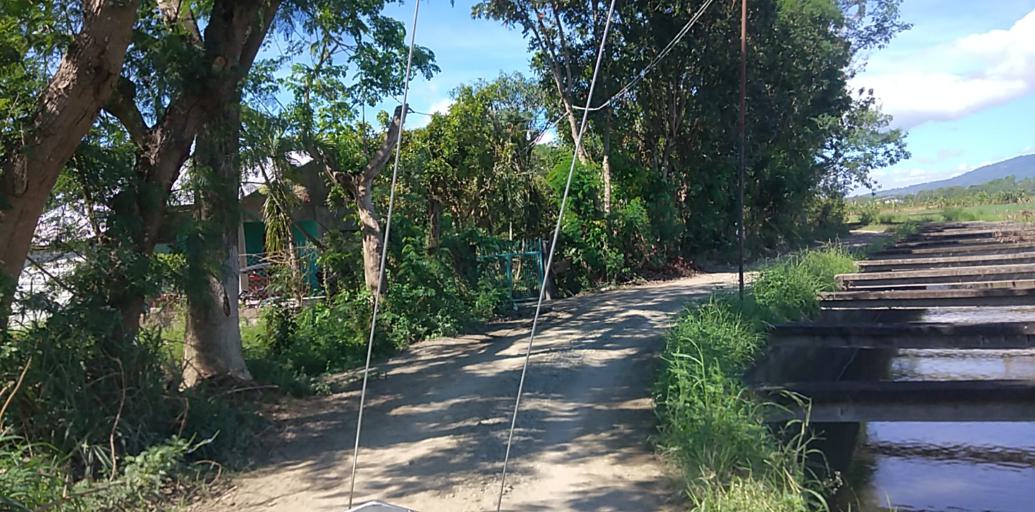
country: PH
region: Central Luzon
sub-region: Province of Pampanga
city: Arayat
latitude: 15.1286
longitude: 120.7896
